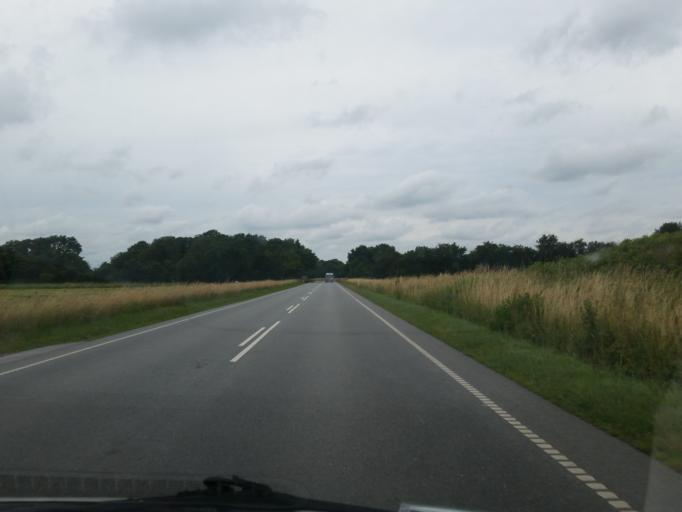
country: DK
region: South Denmark
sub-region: Vejen Kommune
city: Holsted
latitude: 55.4103
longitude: 8.9406
